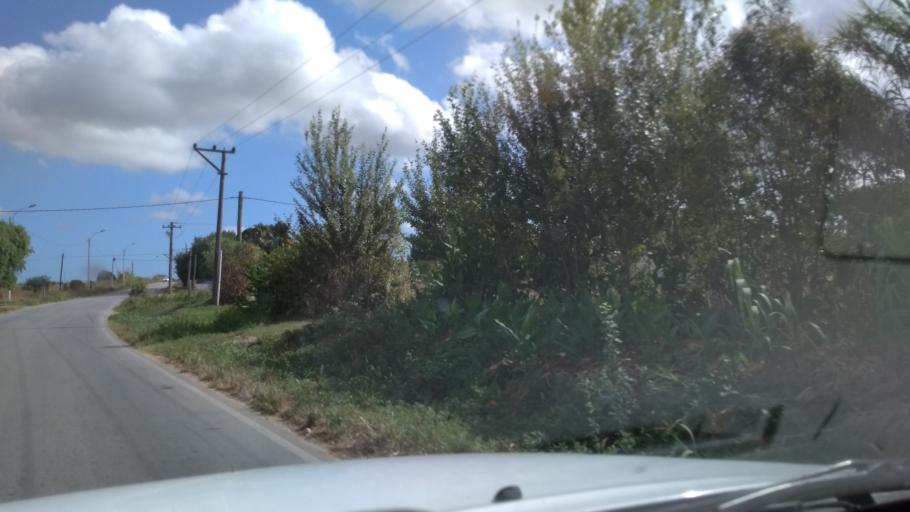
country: UY
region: Canelones
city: Colonia Nicolich
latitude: -34.7786
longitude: -56.0184
